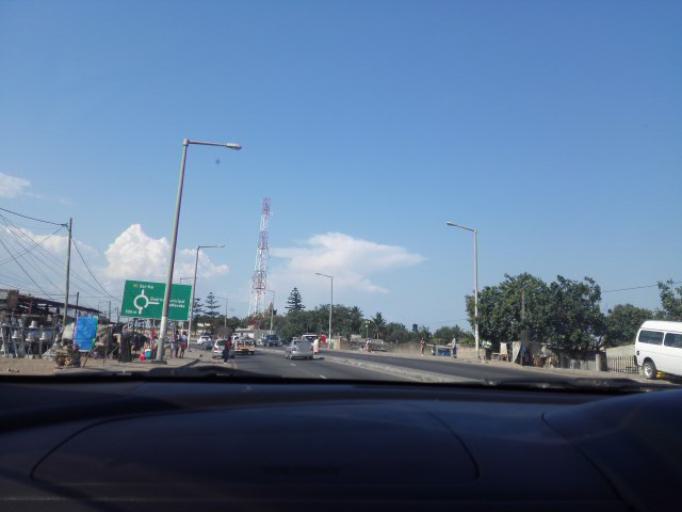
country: MZ
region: Maputo City
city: Maputo
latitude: -25.8822
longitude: 32.5676
